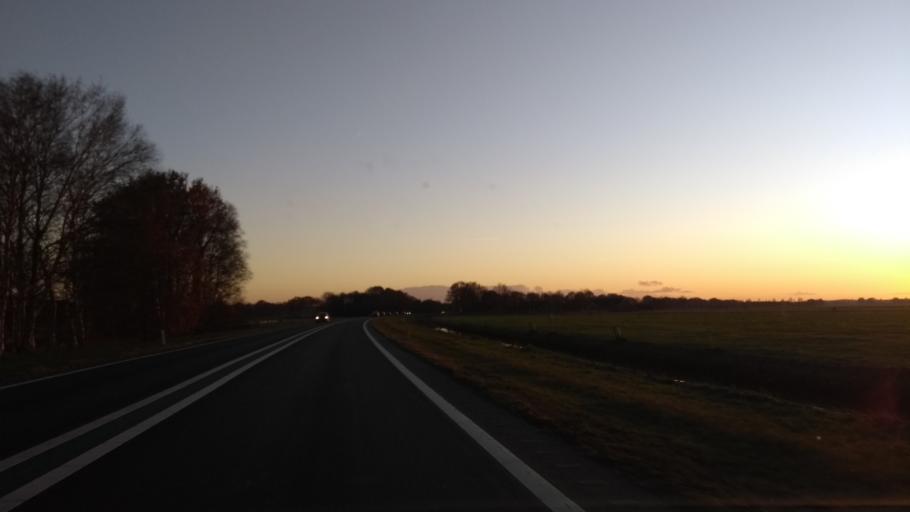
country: NL
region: Overijssel
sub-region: Gemeente Twenterand
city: Den Ham
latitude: 52.5619
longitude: 6.4231
